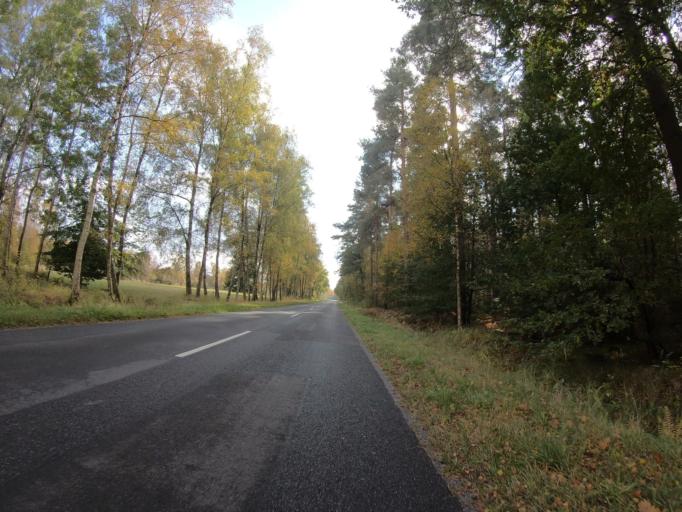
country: DE
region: Lower Saxony
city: Schoneworde
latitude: 52.5952
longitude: 10.6415
